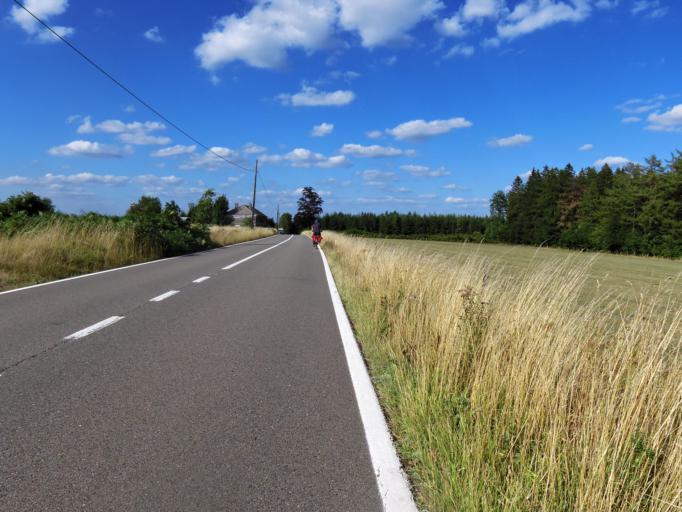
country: BE
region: Wallonia
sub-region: Province de Namur
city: Bievre
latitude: 49.9261
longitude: 5.0414
